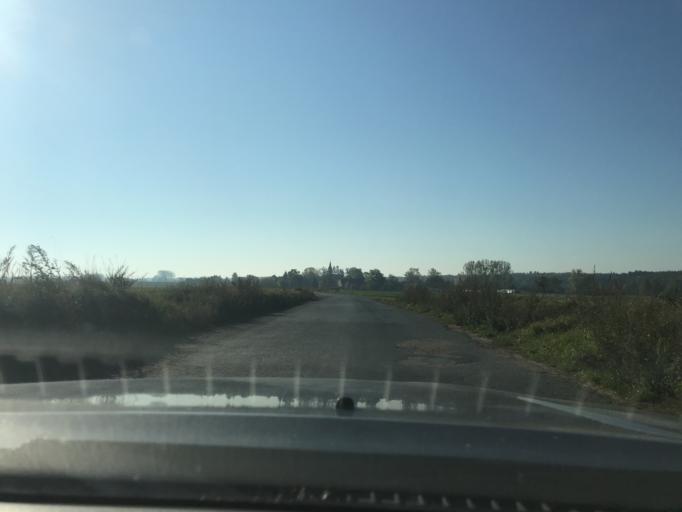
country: PL
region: West Pomeranian Voivodeship
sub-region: Powiat choszczenski
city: Recz
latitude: 53.2201
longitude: 15.5480
